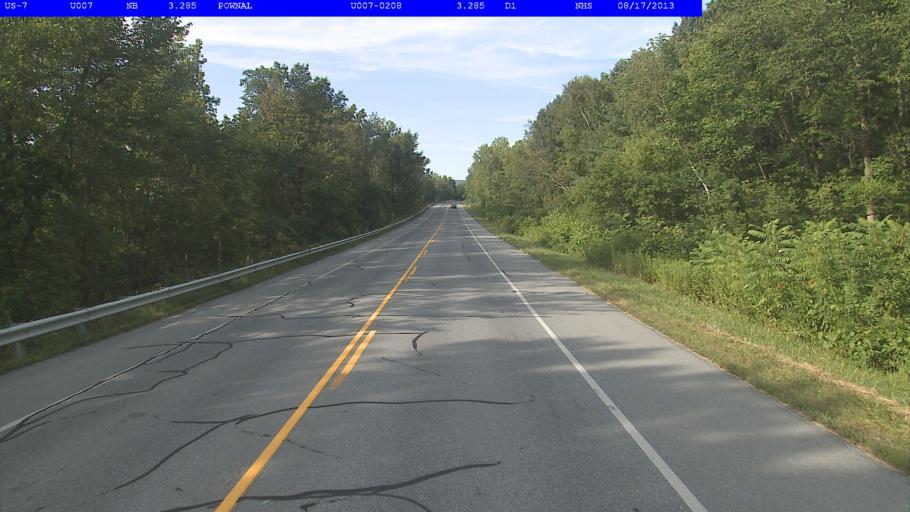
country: US
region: Massachusetts
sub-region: Berkshire County
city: Williamstown
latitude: 42.7822
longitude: -73.2427
